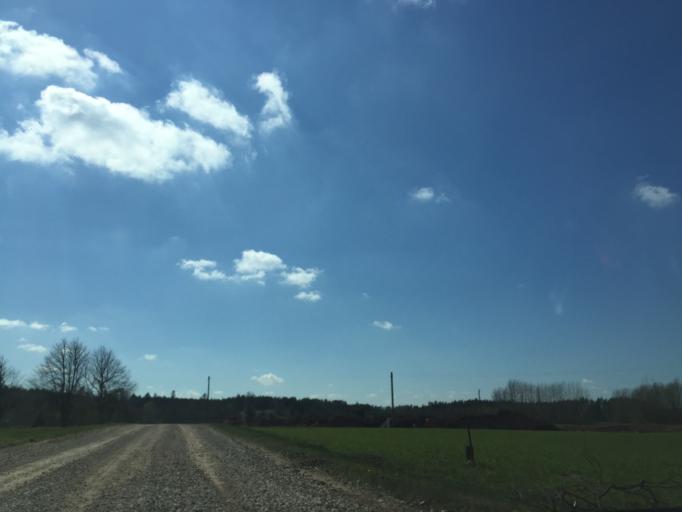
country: LV
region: Smiltene
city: Smiltene
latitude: 57.5854
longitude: 25.9456
